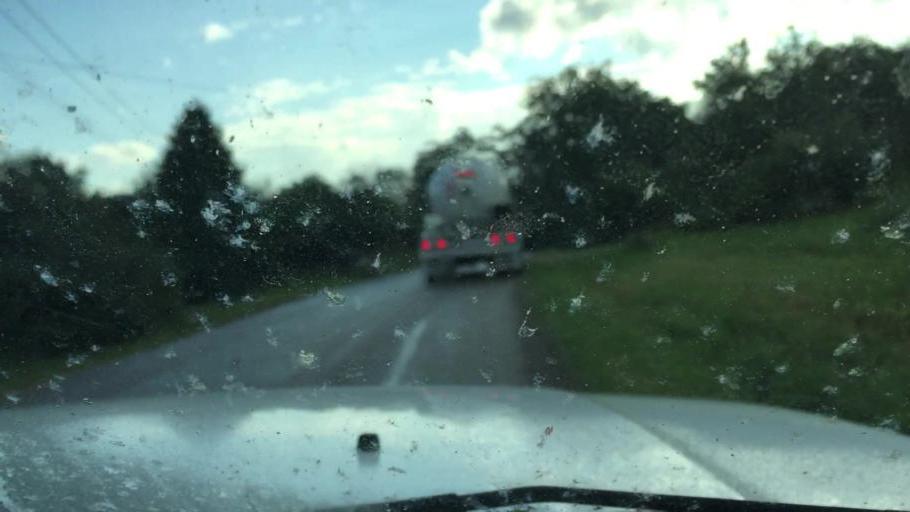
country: US
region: Ohio
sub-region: Champaign County
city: Mechanicsburg
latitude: 40.0252
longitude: -83.6168
